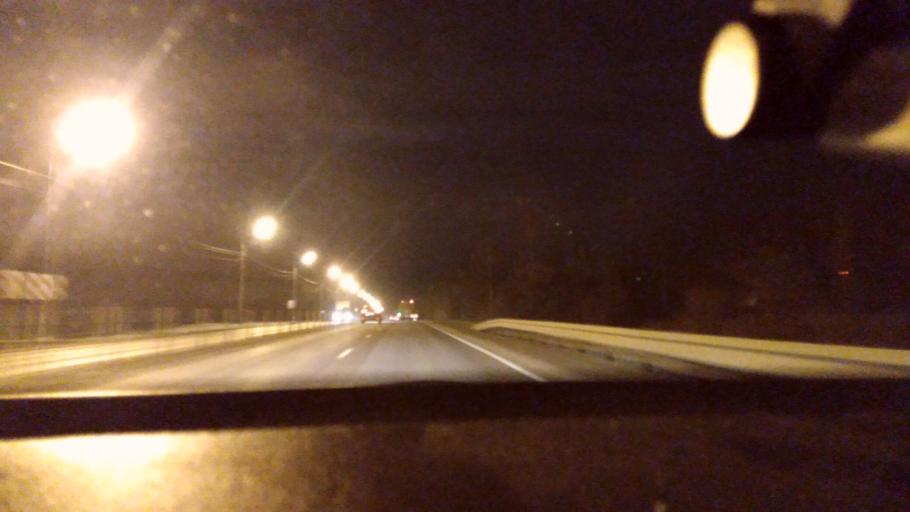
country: RU
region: Moskovskaya
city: Troitskoye
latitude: 55.3312
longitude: 38.4426
